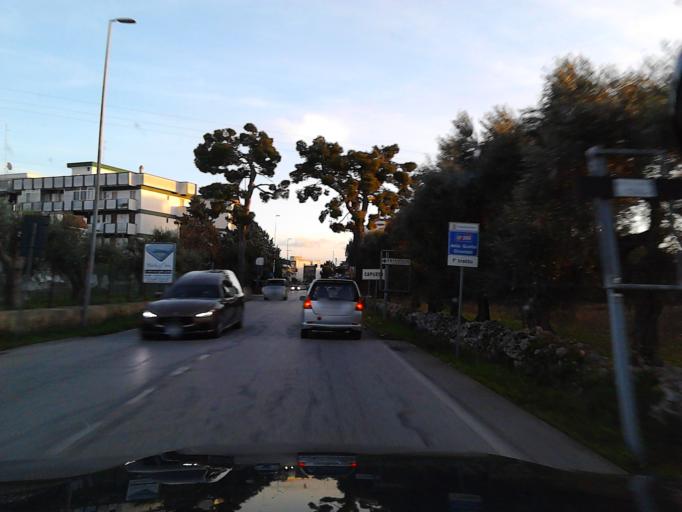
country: IT
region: Apulia
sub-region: Provincia di Bari
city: Capurso
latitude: 41.0524
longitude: 16.9165
